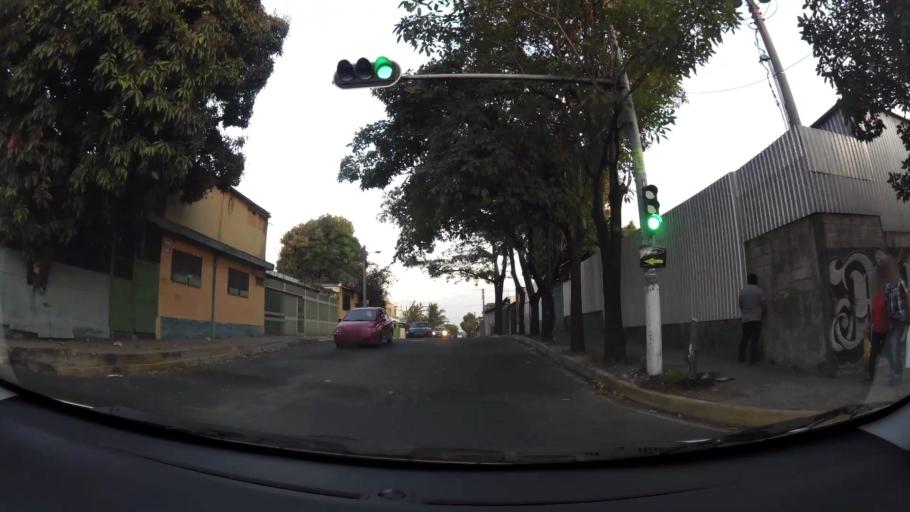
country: SV
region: San Salvador
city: San Salvador
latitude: 13.7114
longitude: -89.1887
